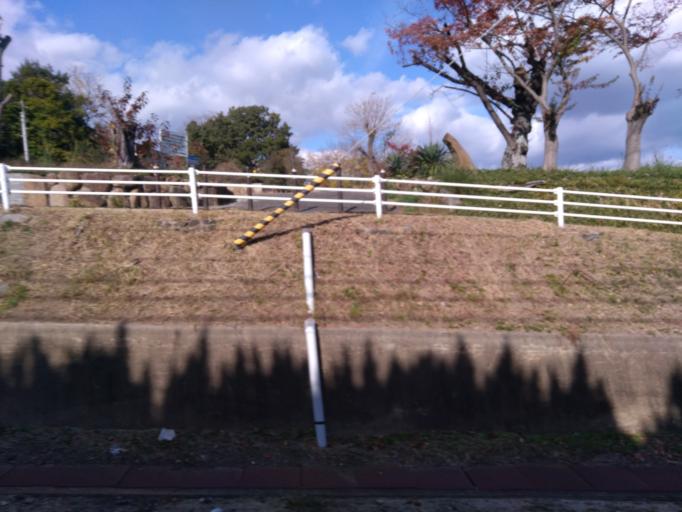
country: JP
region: Hyogo
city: Kawanishi
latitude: 34.8273
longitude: 135.4100
